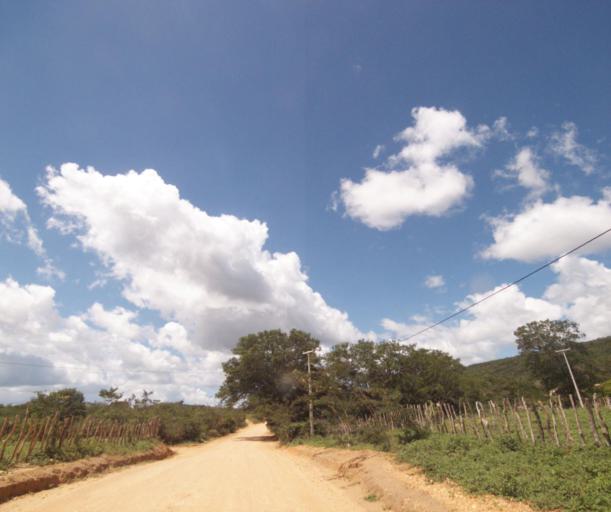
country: BR
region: Bahia
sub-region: Pocoes
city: Pocoes
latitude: -14.3418
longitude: -40.5940
